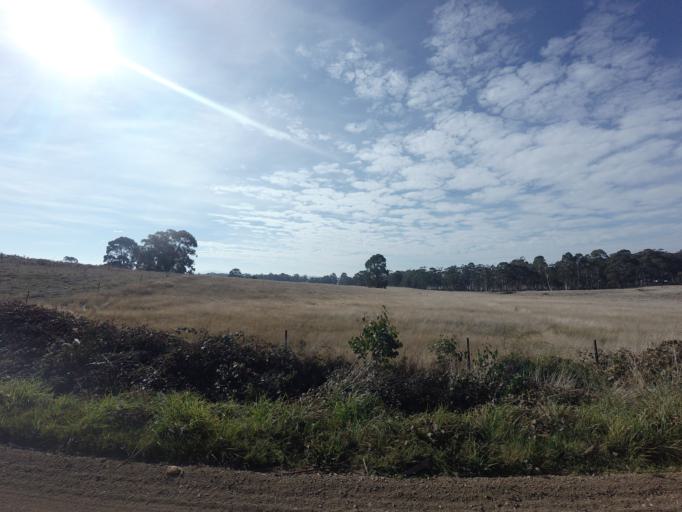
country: AU
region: Tasmania
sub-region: Sorell
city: Sorell
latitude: -42.4747
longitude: 147.4741
